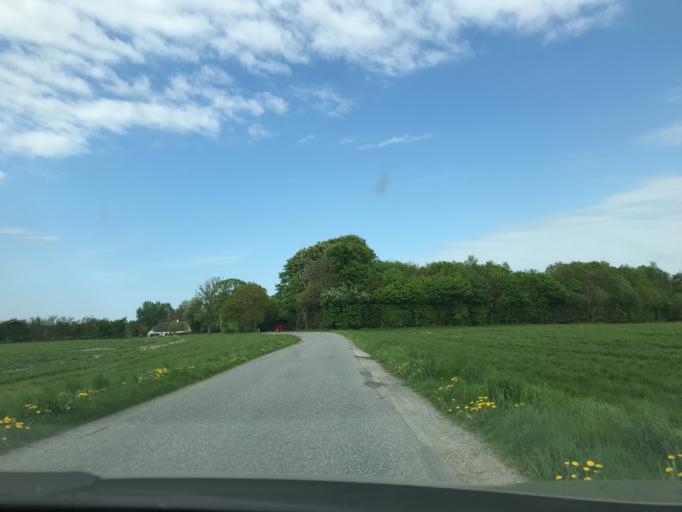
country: DK
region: South Denmark
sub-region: Middelfart Kommune
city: Norre Aby
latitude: 55.3983
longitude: 9.8611
